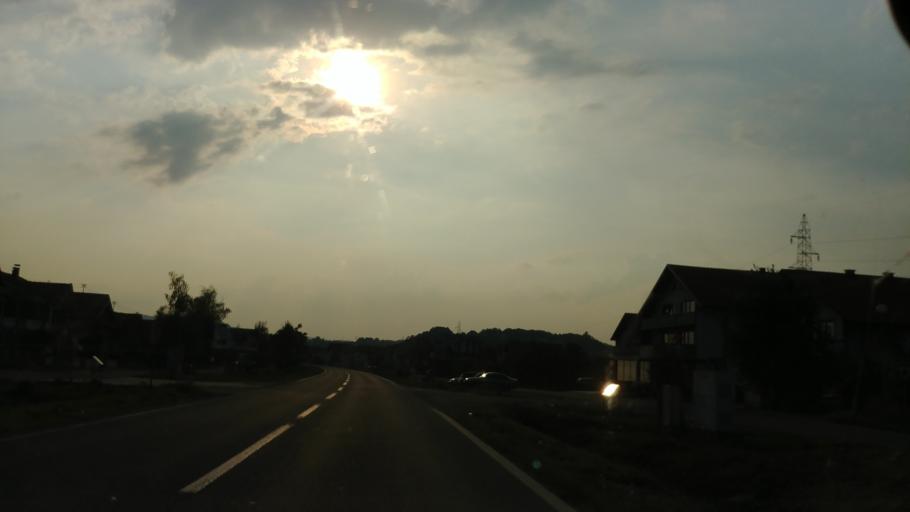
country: BA
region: Republika Srpska
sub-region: Opstina Ugljevik
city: Ugljevik
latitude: 44.6970
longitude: 19.0039
